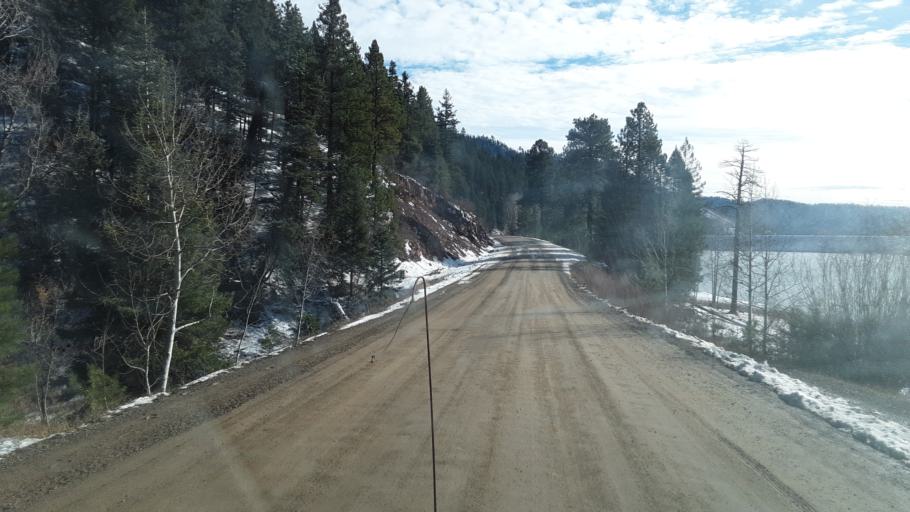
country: US
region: Colorado
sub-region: La Plata County
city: Bayfield
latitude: 37.3946
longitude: -107.6573
